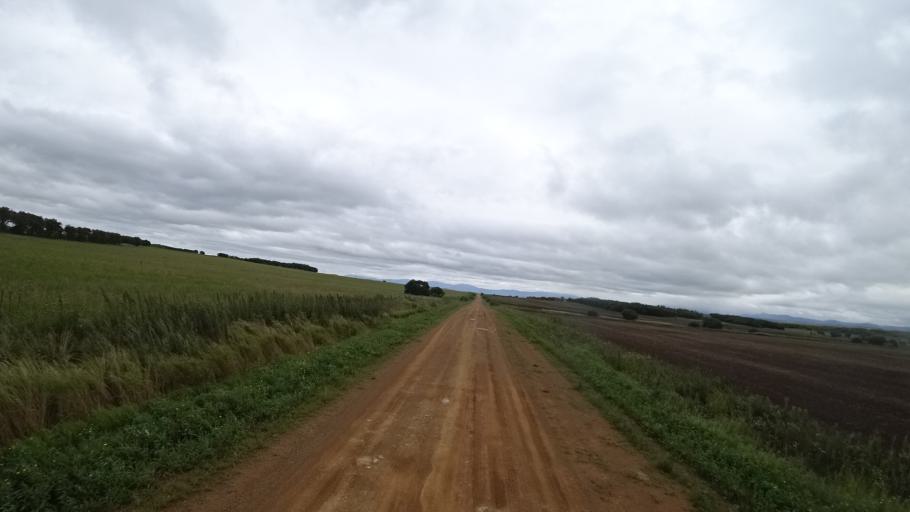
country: RU
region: Primorskiy
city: Chernigovka
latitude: 44.4368
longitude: 132.5831
